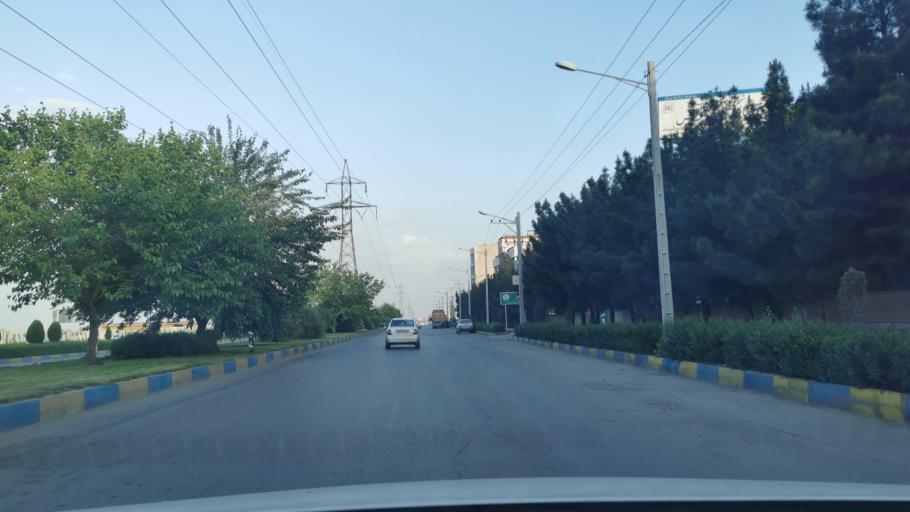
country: IR
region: Razavi Khorasan
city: Torqabeh
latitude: 36.4237
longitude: 59.4252
